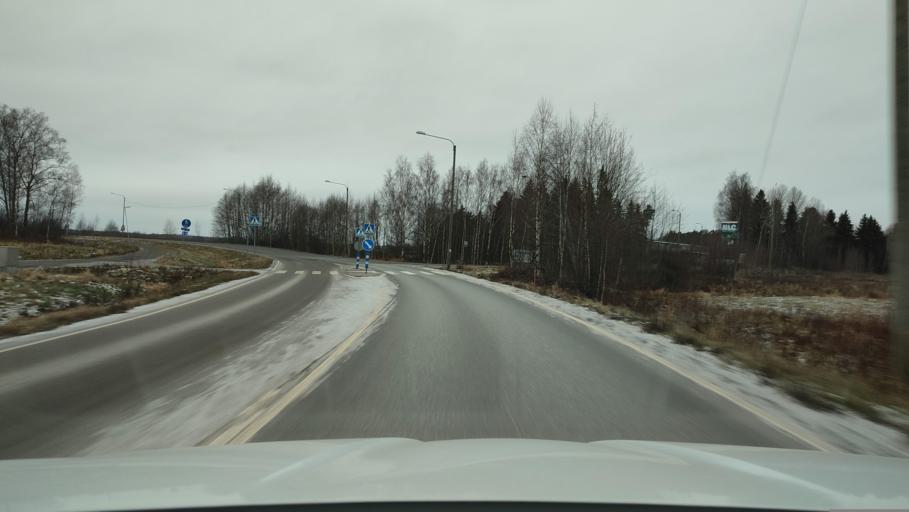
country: FI
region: Ostrobothnia
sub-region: Vaasa
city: Ristinummi
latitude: 63.0363
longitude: 21.7835
